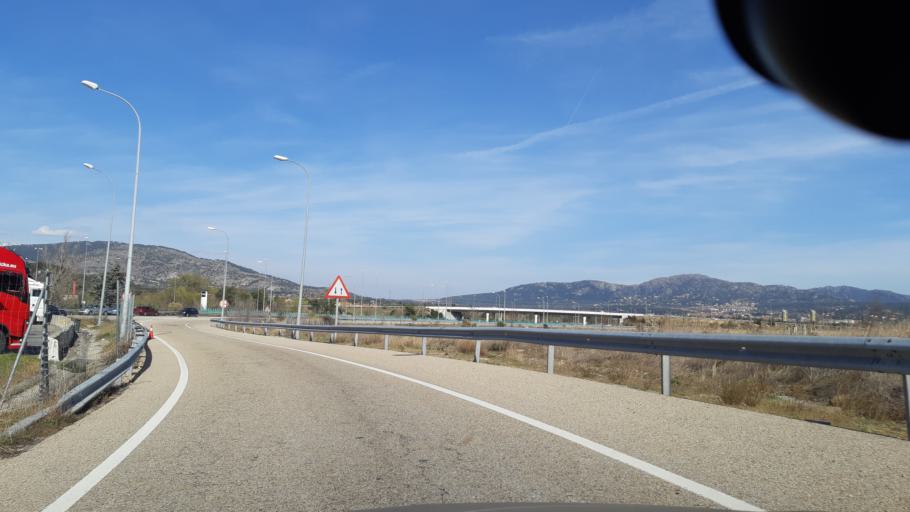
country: ES
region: Madrid
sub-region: Provincia de Madrid
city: Alpedrete
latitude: 40.6416
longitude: -4.0390
